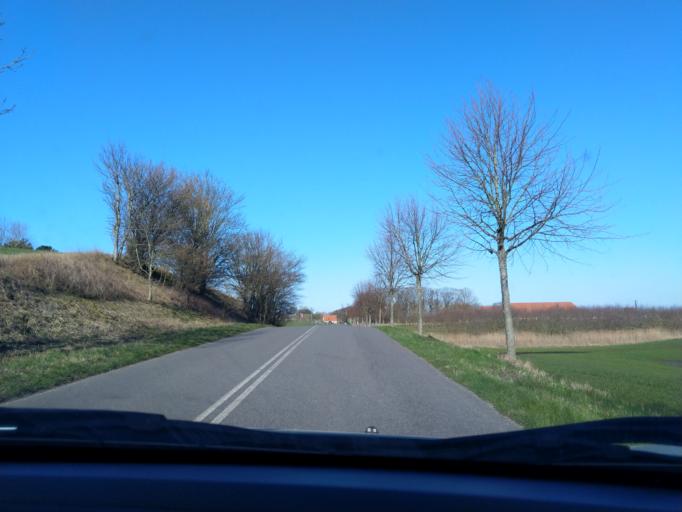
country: DK
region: Zealand
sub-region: Kalundborg Kommune
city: Kalundborg
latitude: 55.7309
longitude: 10.9833
